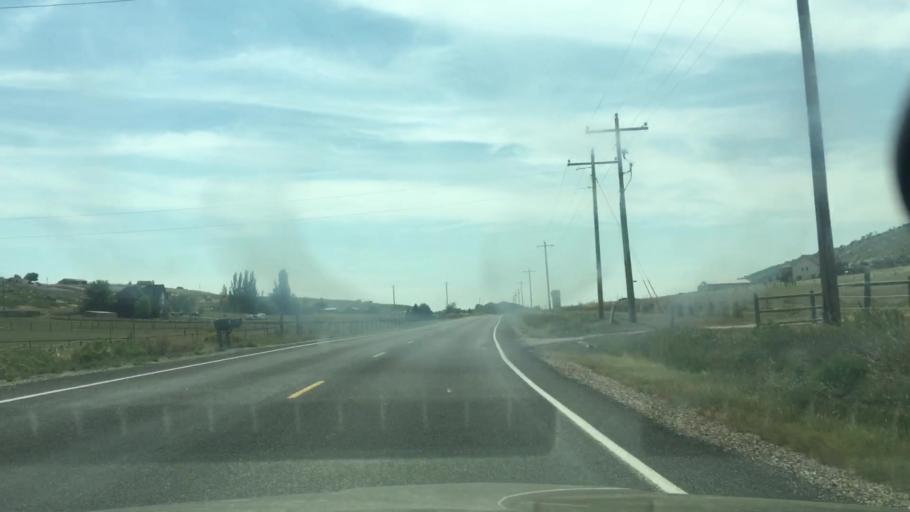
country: US
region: Colorado
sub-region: Larimer County
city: Campion
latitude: 40.3543
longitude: -105.1847
